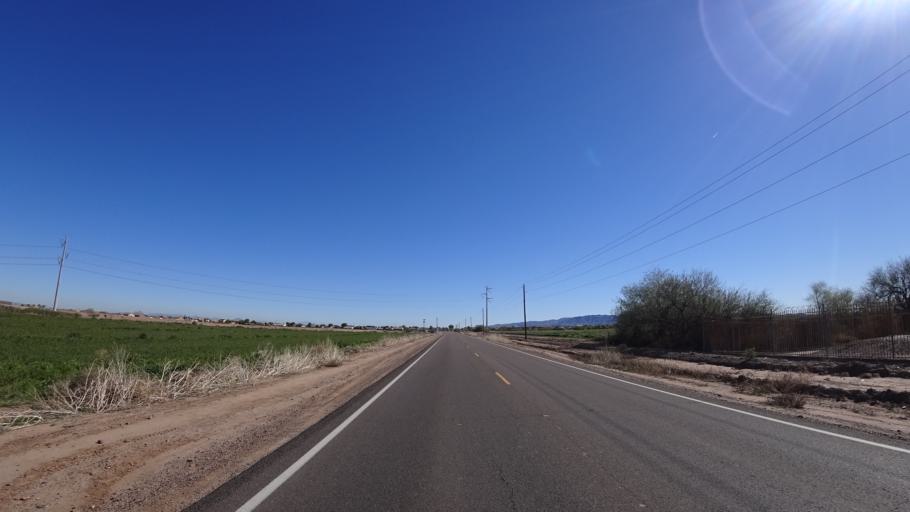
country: US
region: Arizona
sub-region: Maricopa County
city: Laveen
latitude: 33.3773
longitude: -112.2262
